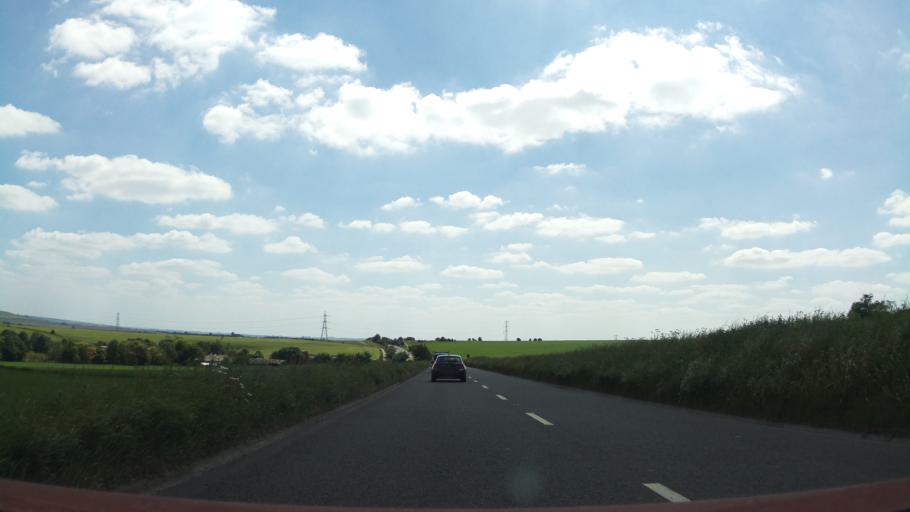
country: GB
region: England
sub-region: Wiltshire
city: Devizes
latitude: 51.3809
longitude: -1.9539
